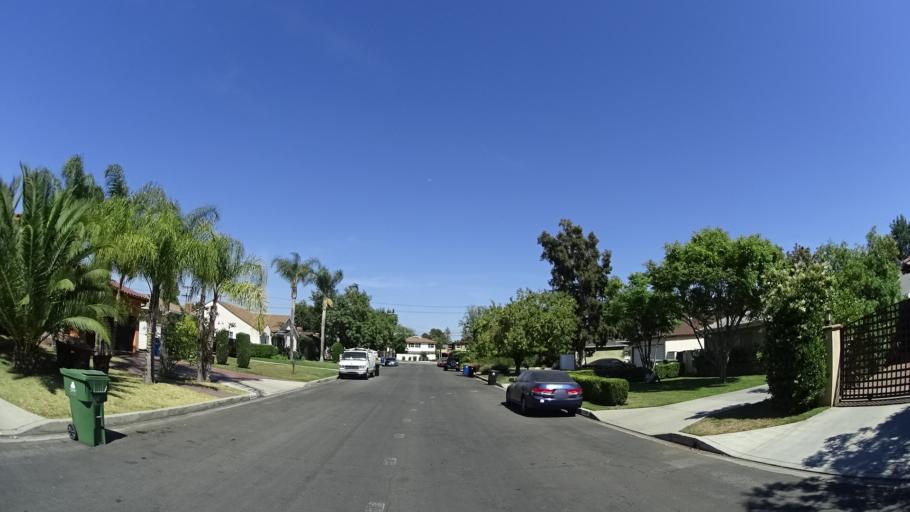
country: US
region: California
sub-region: Los Angeles County
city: North Hollywood
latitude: 34.1739
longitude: -118.4065
